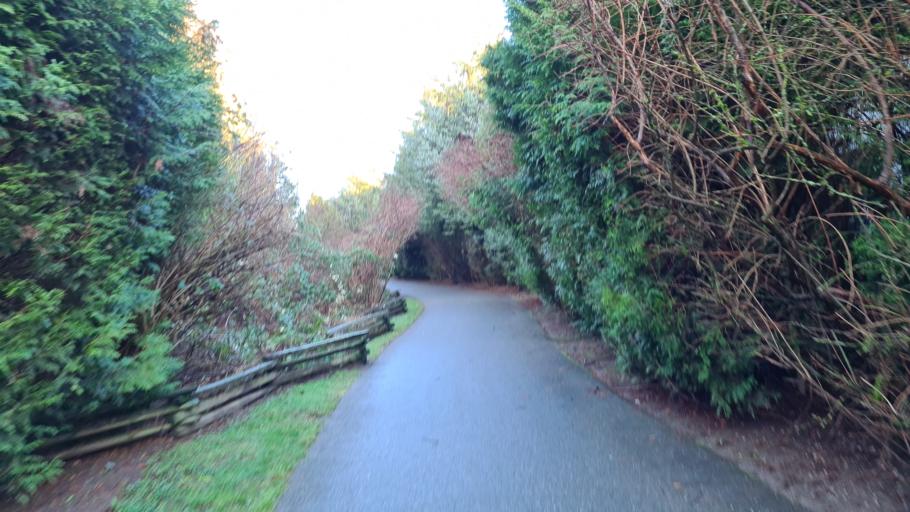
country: CA
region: British Columbia
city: Langley
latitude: 49.1285
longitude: -122.6711
